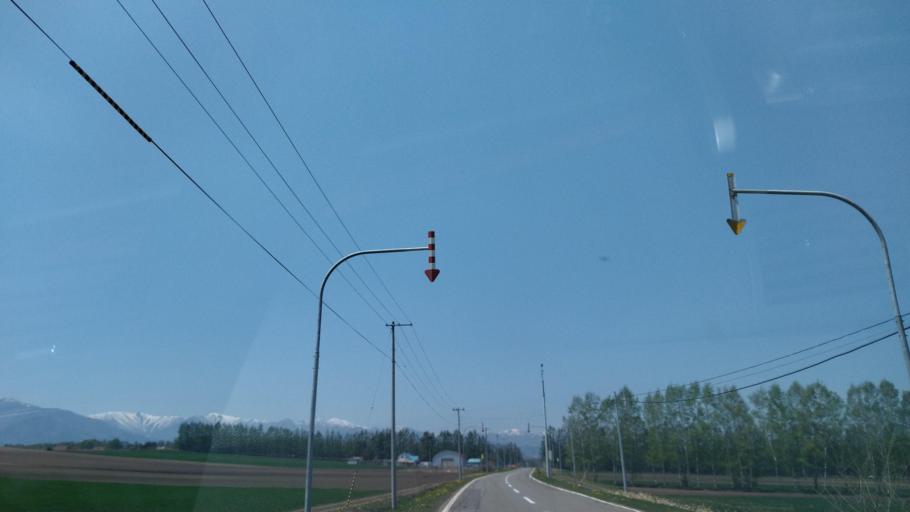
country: JP
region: Hokkaido
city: Obihiro
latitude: 42.9049
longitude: 142.9995
